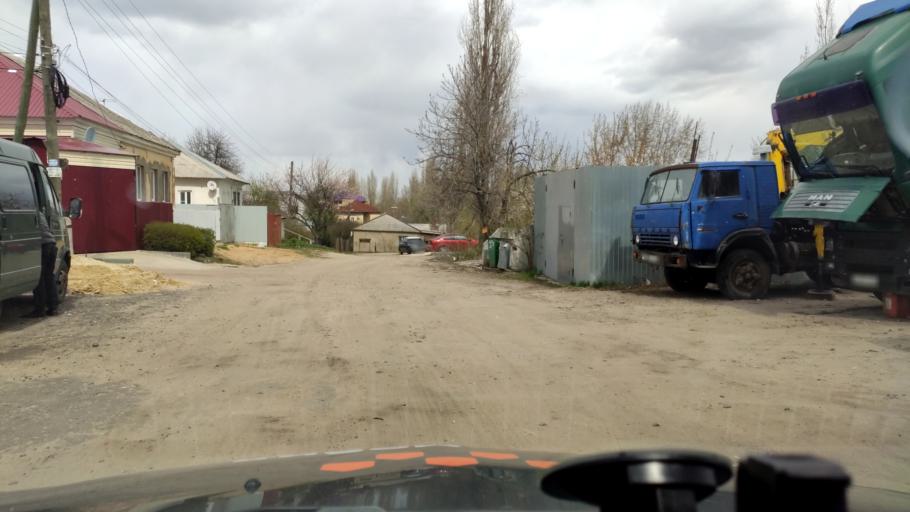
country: RU
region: Voronezj
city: Voronezh
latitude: 51.6312
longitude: 39.2041
